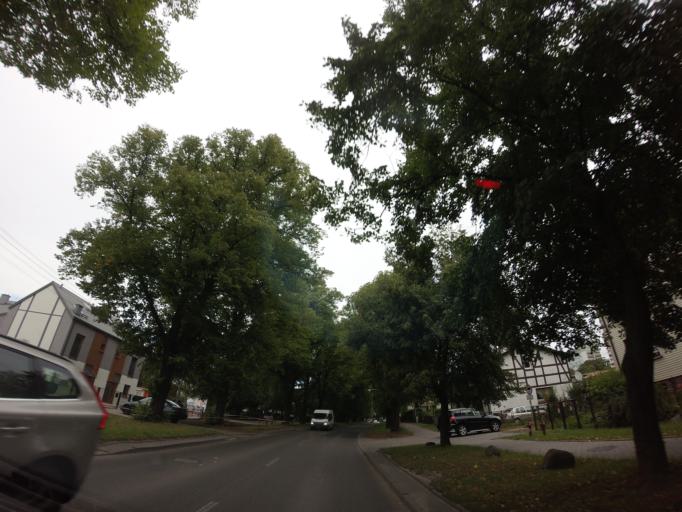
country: PL
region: West Pomeranian Voivodeship
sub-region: Szczecin
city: Szczecin
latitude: 53.4517
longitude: 14.4839
